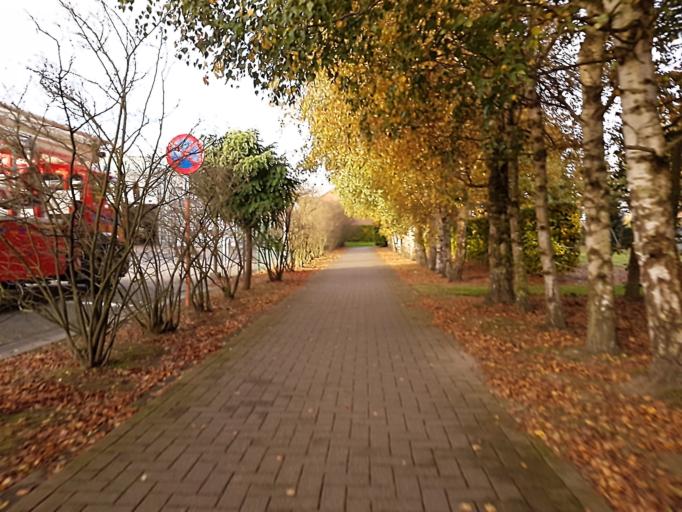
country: BE
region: Flanders
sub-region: Provincie Antwerpen
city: Ranst
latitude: 51.1848
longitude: 4.5910
